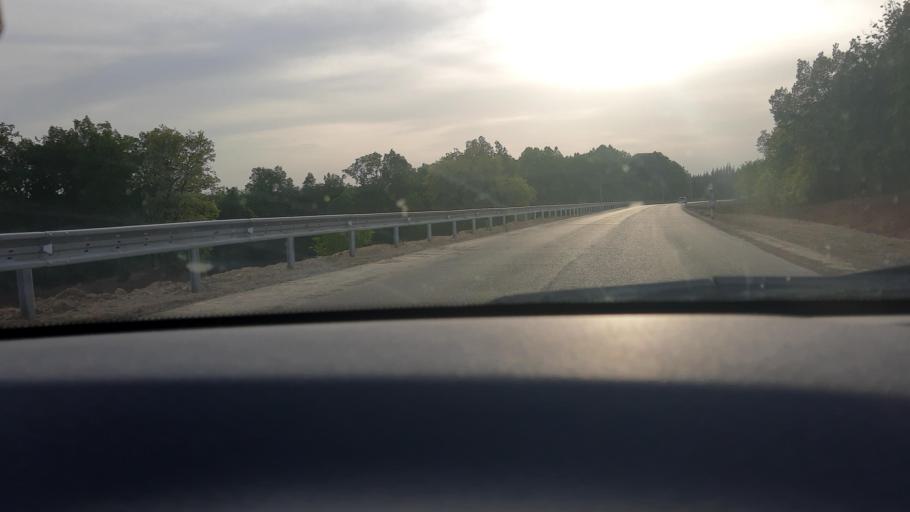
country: RU
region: Bashkortostan
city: Iglino
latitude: 54.8033
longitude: 56.4725
